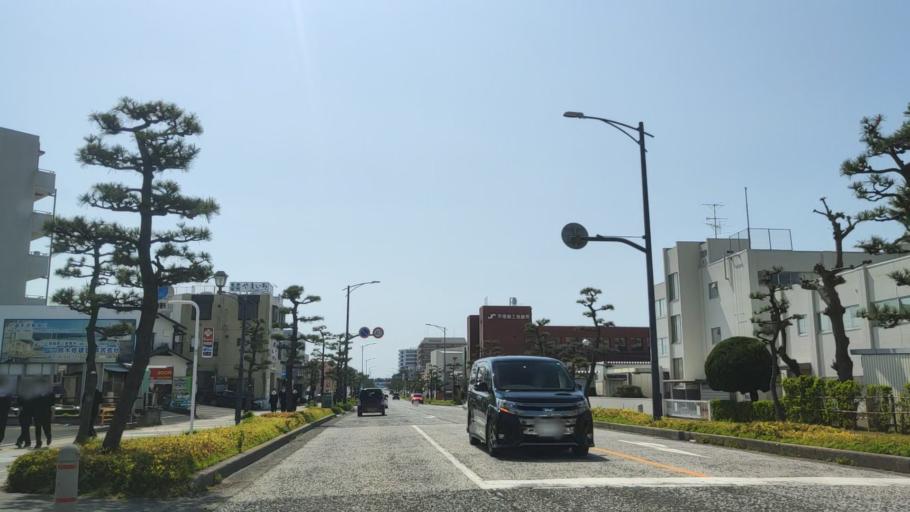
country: JP
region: Kanagawa
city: Hiratsuka
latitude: 35.3245
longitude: 139.3522
